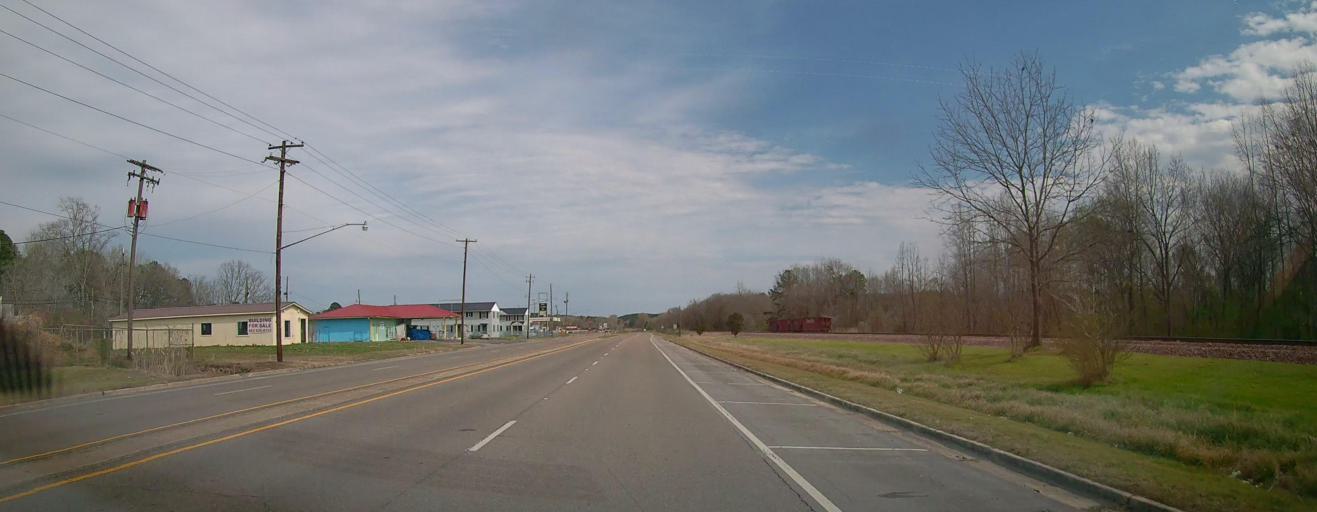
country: US
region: Alabama
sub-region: Walker County
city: Carbon Hill
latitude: 33.8871
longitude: -87.5251
